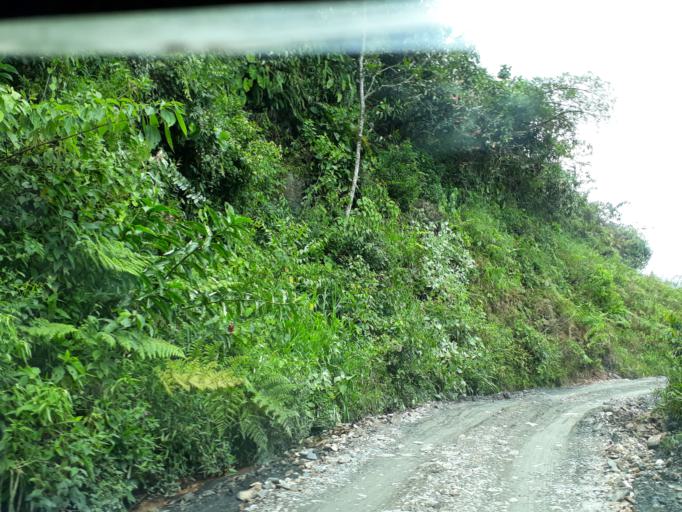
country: CO
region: Cundinamarca
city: Topaipi
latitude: 5.3438
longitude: -74.1871
